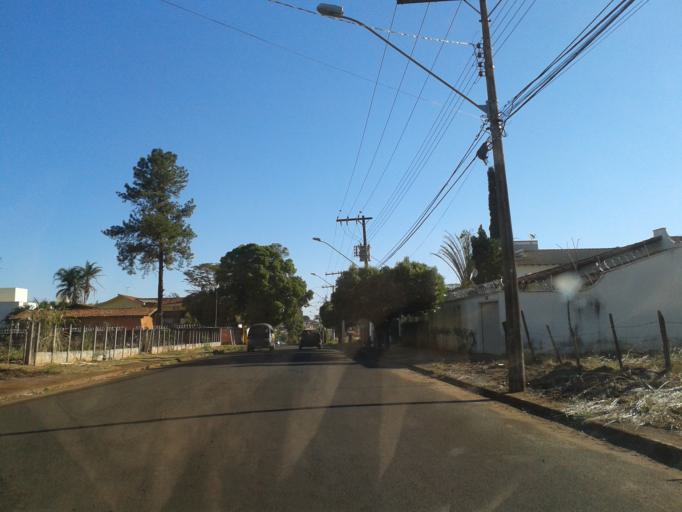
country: BR
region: Minas Gerais
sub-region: Ituiutaba
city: Ituiutaba
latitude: -18.9695
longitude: -49.4471
